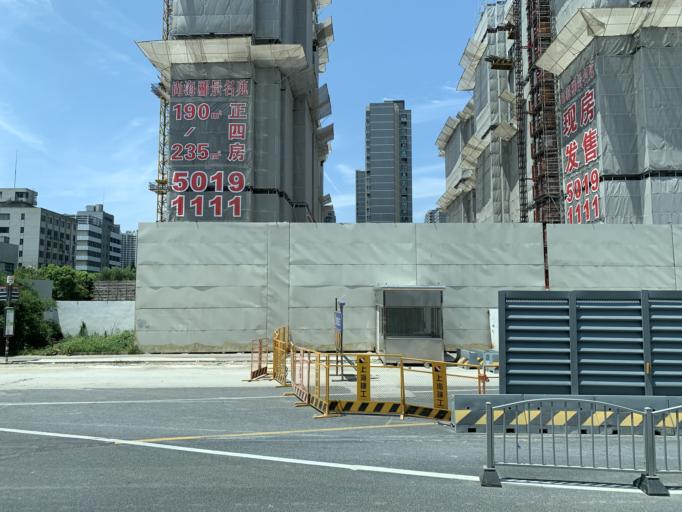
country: CN
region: Shanghai Shi
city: Pudong
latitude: 31.2424
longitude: 121.5378
